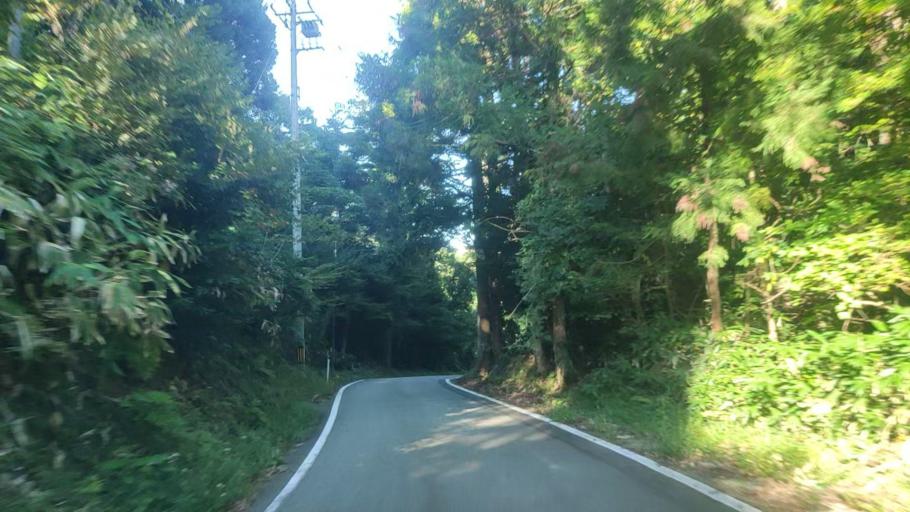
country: JP
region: Ishikawa
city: Nanao
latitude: 37.1177
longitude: 136.8914
